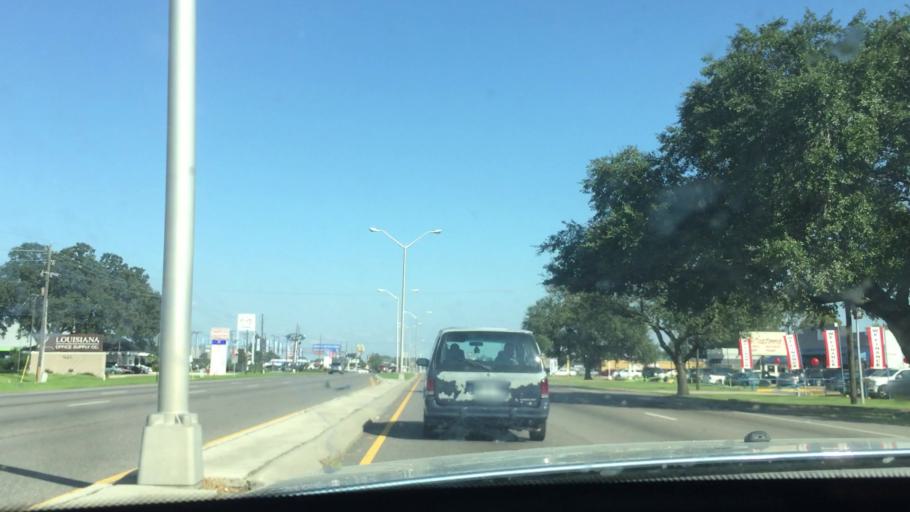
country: US
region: Louisiana
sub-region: East Baton Rouge Parish
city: Baton Rouge
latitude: 30.4517
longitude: -91.1113
